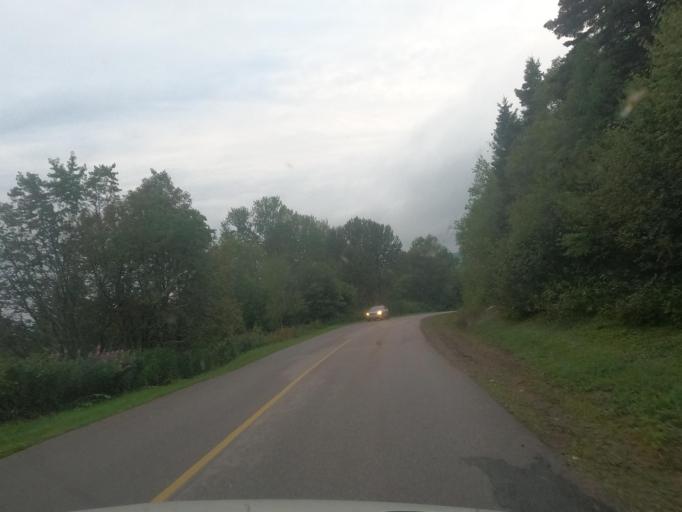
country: CA
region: Ontario
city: Marathon
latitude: 48.7783
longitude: -87.1040
